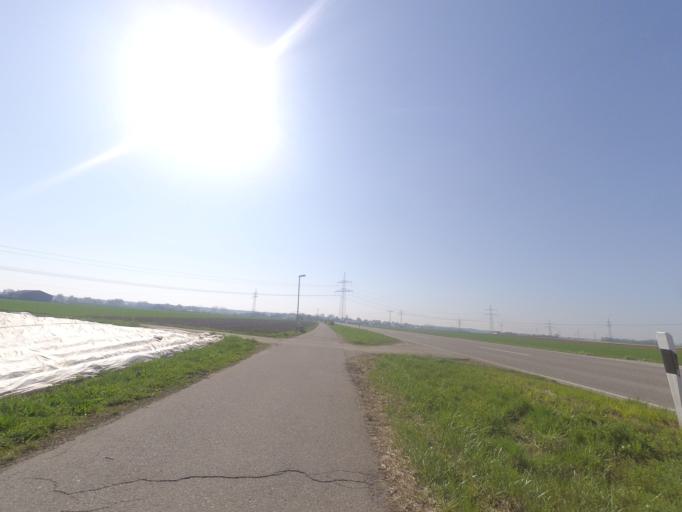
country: DE
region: Bavaria
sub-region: Swabia
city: Nersingen
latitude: 48.4236
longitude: 10.1280
